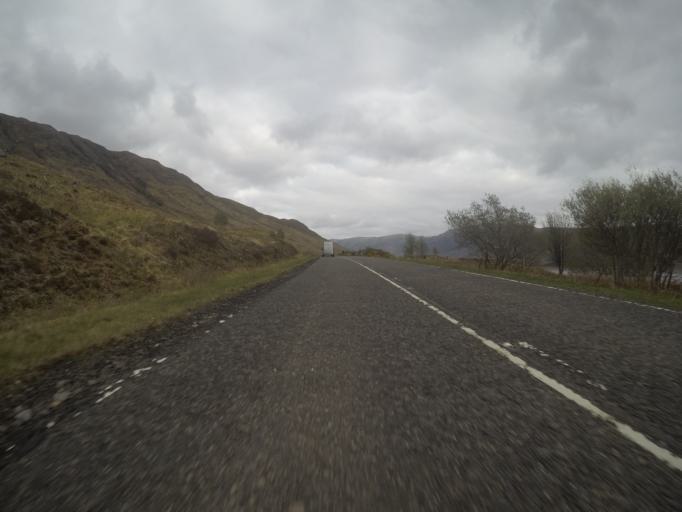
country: GB
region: Scotland
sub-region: Highland
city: Fort William
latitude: 57.1542
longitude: -5.1359
